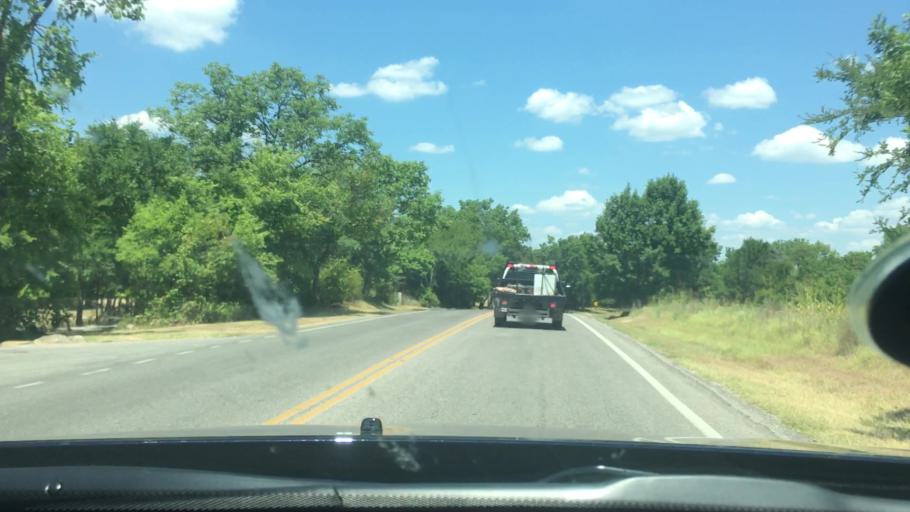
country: US
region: Oklahoma
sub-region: Murray County
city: Sulphur
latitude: 34.4989
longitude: -96.9711
